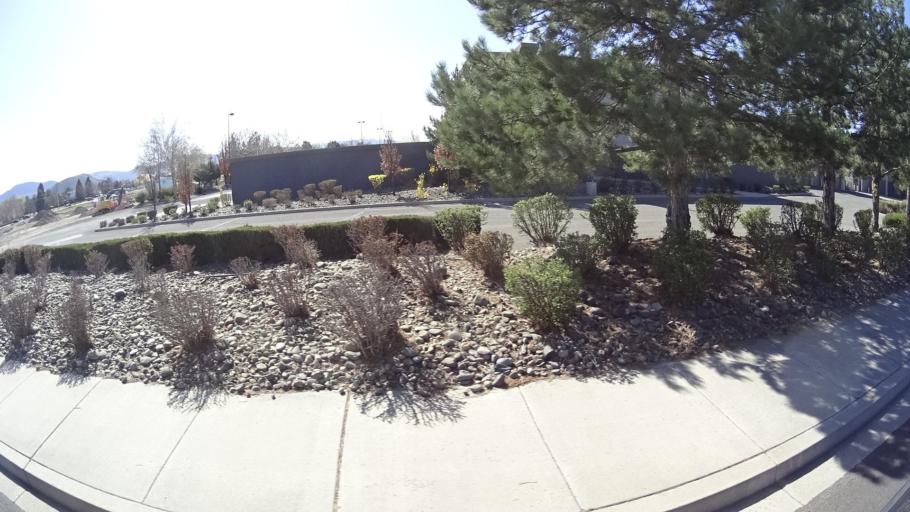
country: US
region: Nevada
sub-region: Washoe County
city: Reno
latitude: 39.4837
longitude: -119.7951
